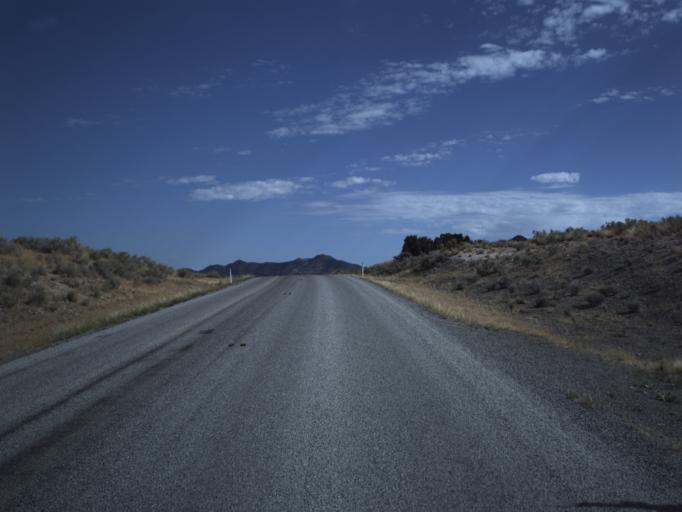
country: US
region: Utah
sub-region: Juab County
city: Mona
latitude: 39.7999
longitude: -112.1454
